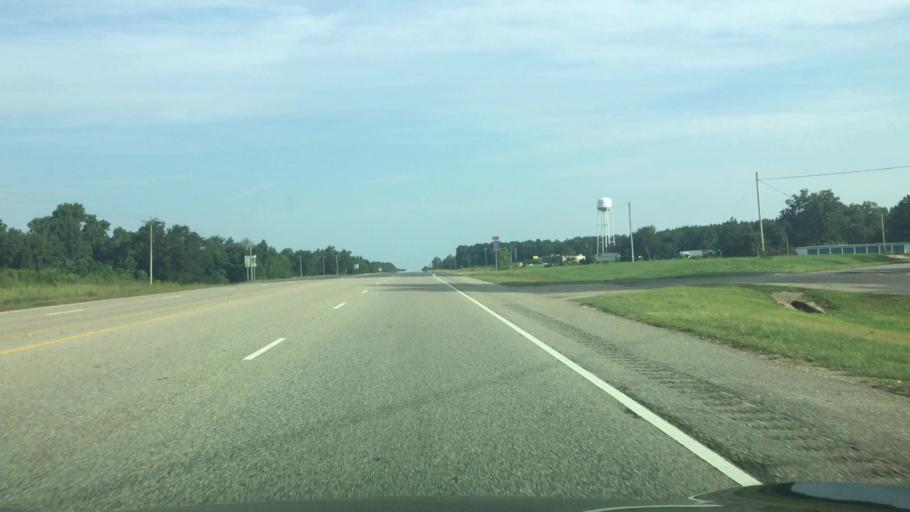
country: US
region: Alabama
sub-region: Butler County
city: Georgiana
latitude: 31.5272
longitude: -86.7185
